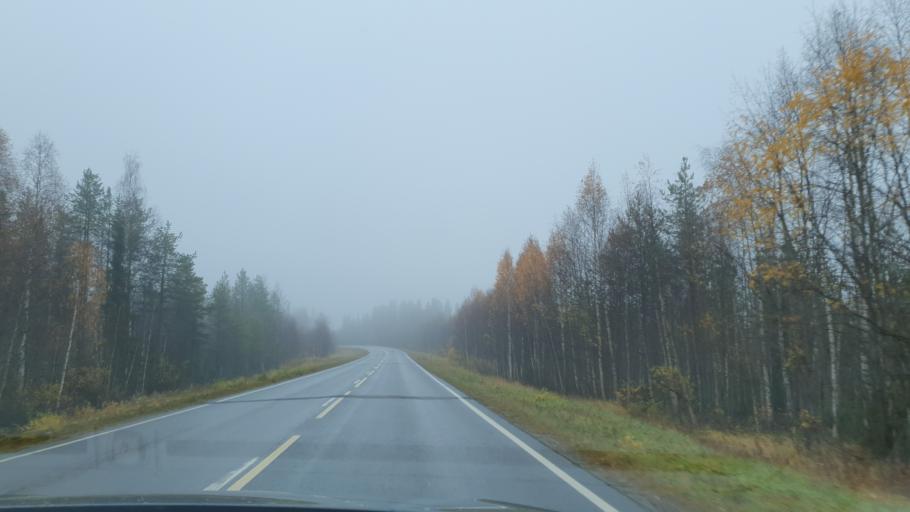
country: FI
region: Lapland
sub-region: Tunturi-Lappi
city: Kittilae
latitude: 67.6630
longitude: 24.8466
